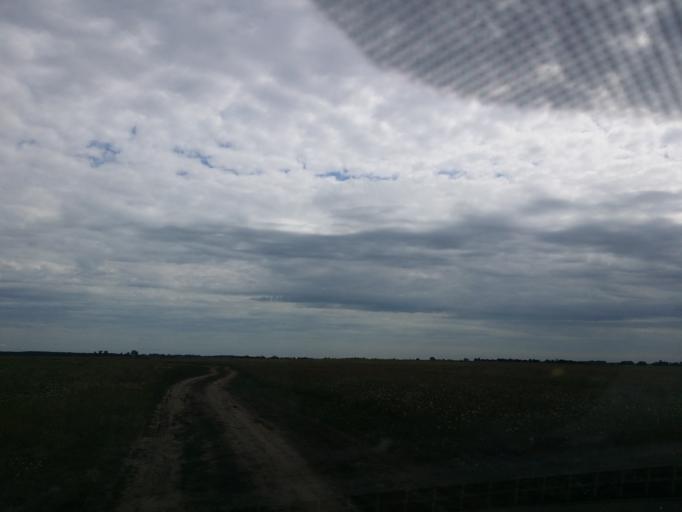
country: HU
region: Hajdu-Bihar
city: Egyek
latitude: 47.5513
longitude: 20.9404
